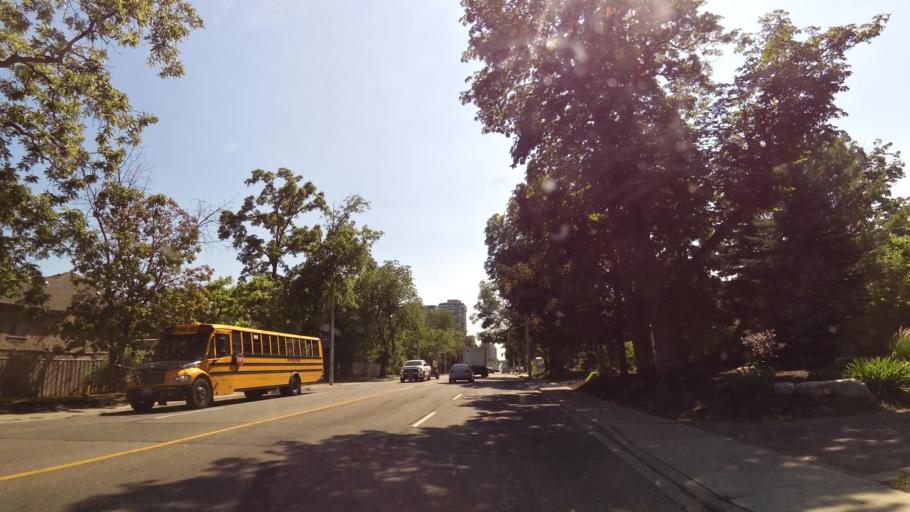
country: CA
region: Ontario
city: Etobicoke
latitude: 43.6541
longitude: -79.5241
